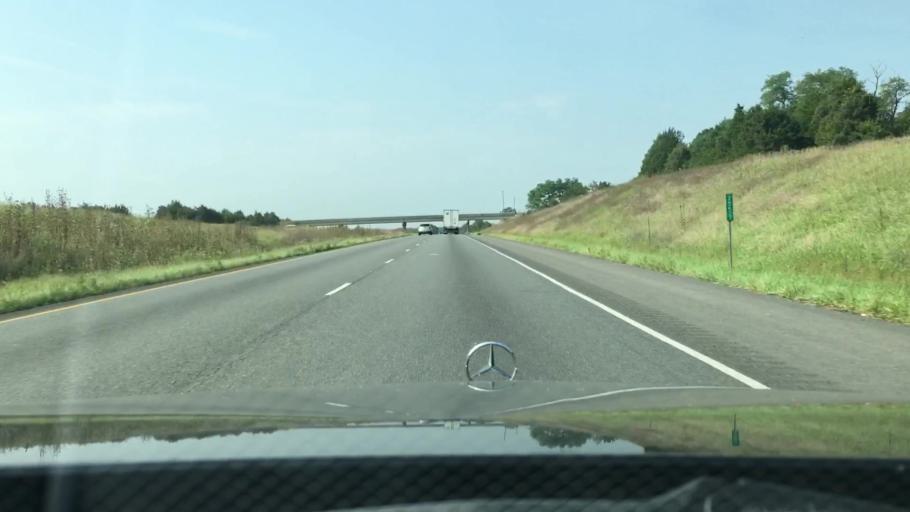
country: US
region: Virginia
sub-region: Rockingham County
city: Broadway
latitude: 38.5389
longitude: -78.7648
